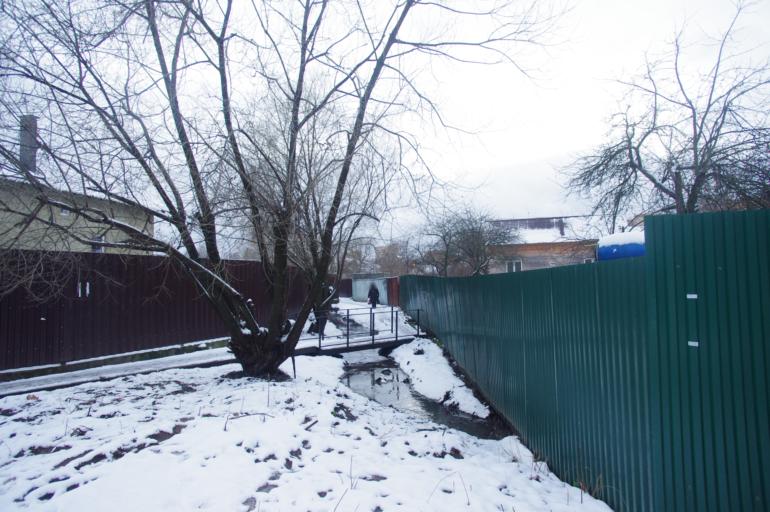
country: RU
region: Moskovskaya
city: Pavshino
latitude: 55.8133
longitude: 37.3520
